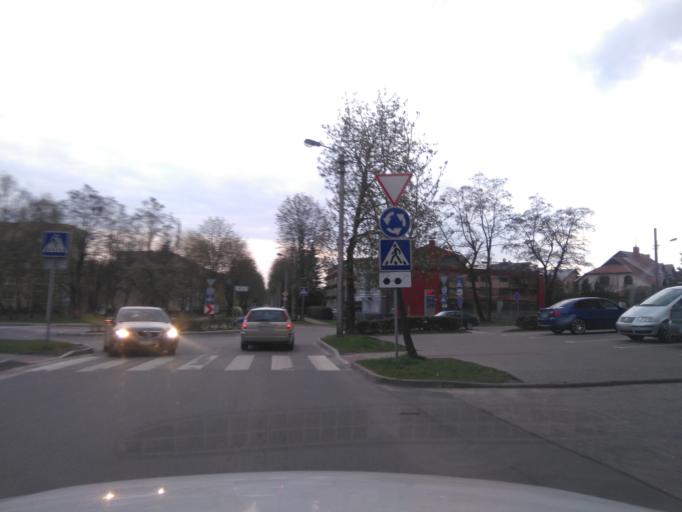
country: LT
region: Kauno apskritis
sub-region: Kaunas
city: Eiguliai
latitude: 54.9087
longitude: 23.9416
